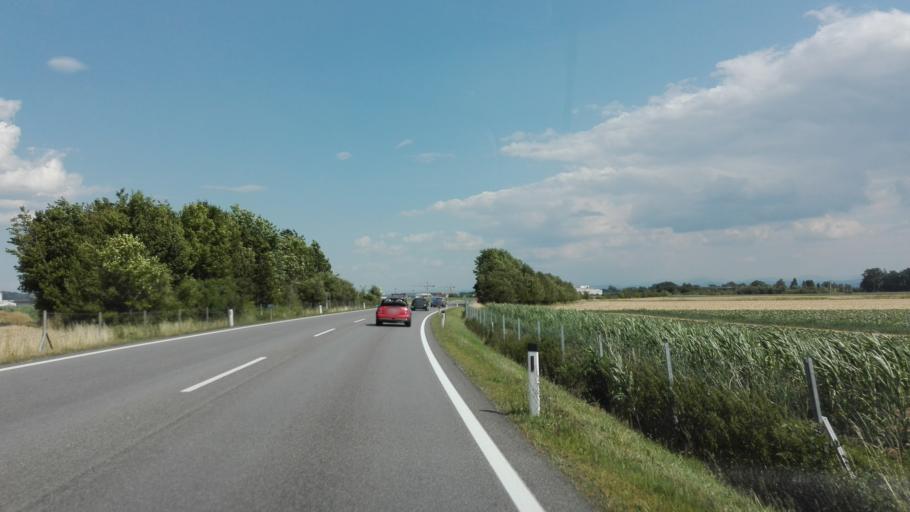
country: AT
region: Upper Austria
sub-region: Politischer Bezirk Perg
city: Perg
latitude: 48.2489
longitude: 14.6032
